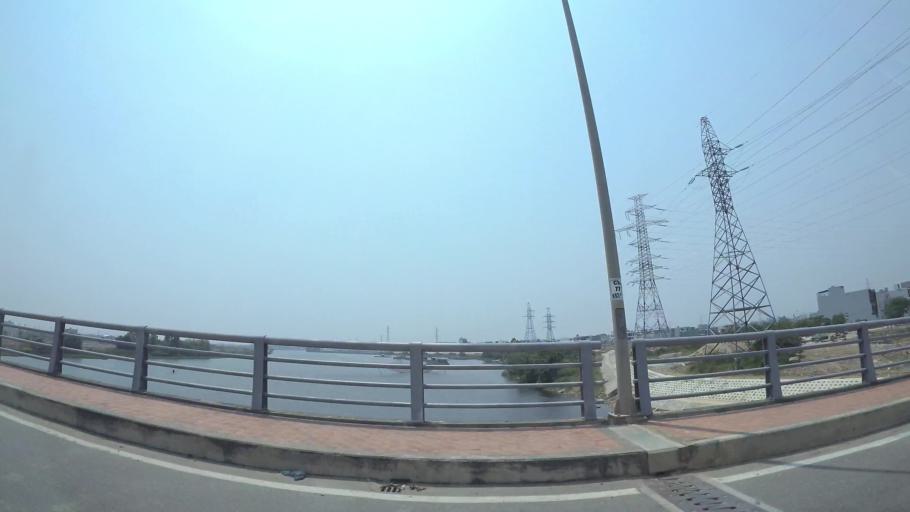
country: VN
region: Da Nang
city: Ngu Hanh Son
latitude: 16.0155
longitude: 108.2346
